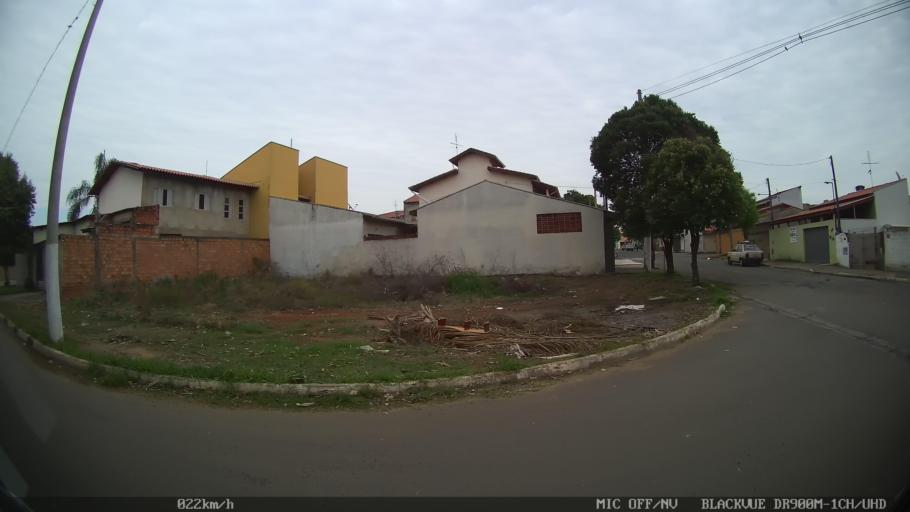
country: BR
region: Sao Paulo
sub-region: Paulinia
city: Paulinia
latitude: -22.7220
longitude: -47.1698
